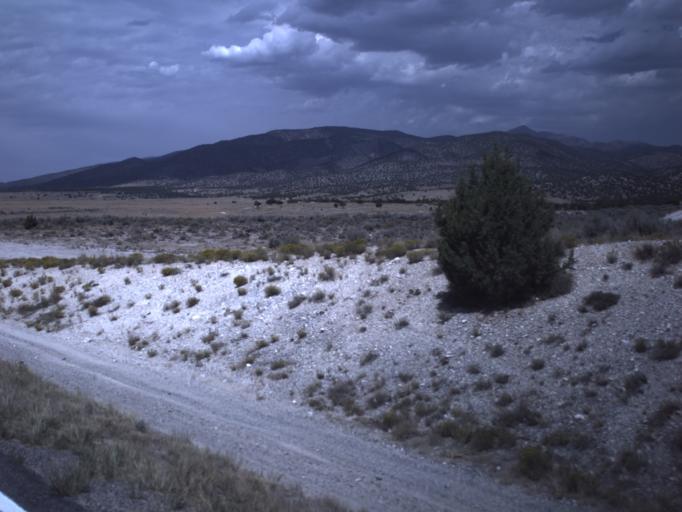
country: US
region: Utah
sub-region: Utah County
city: Eagle Mountain
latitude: 40.2395
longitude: -112.2034
